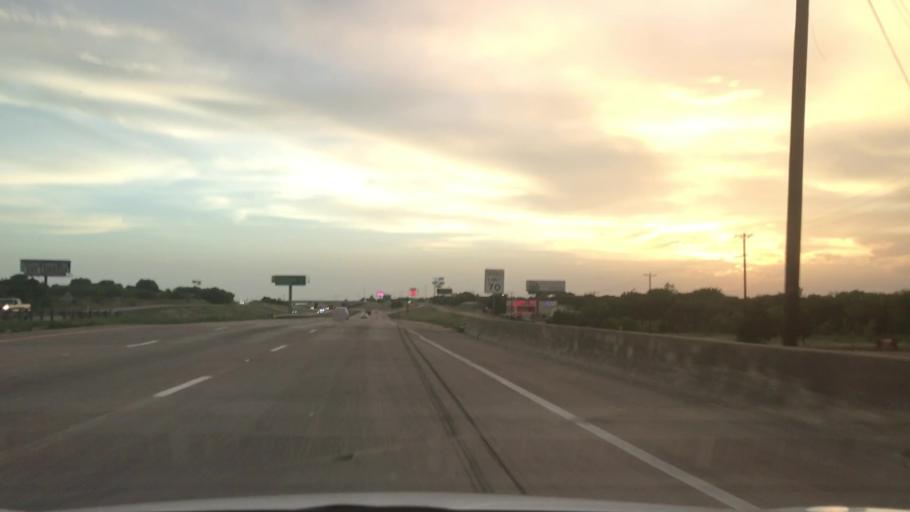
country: US
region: Texas
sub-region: Dallas County
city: Balch Springs
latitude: 32.7043
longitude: -96.5763
